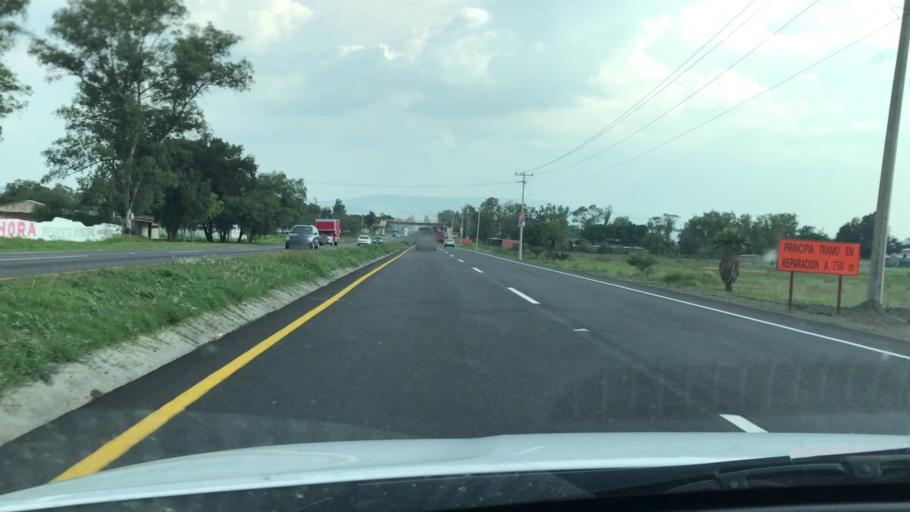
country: MX
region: Guanajuato
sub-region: Irapuato
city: San Ignacio de Rivera (Ojo de Agua)
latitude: 20.5423
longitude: -101.4560
